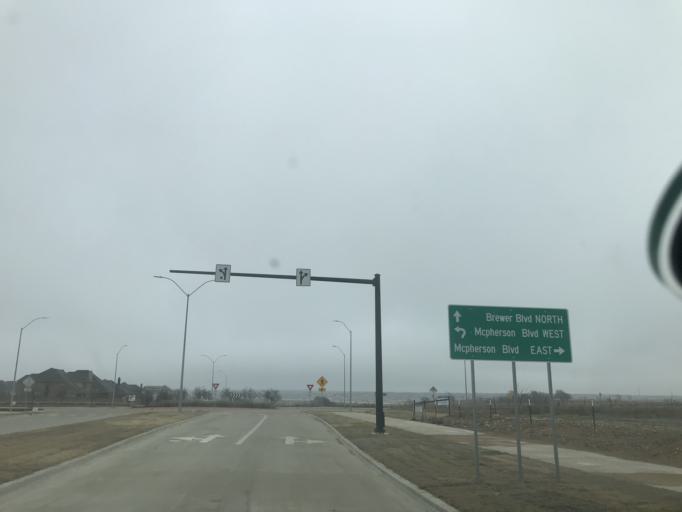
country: US
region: Texas
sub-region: Tarrant County
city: Crowley
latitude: 32.6069
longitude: -97.4209
